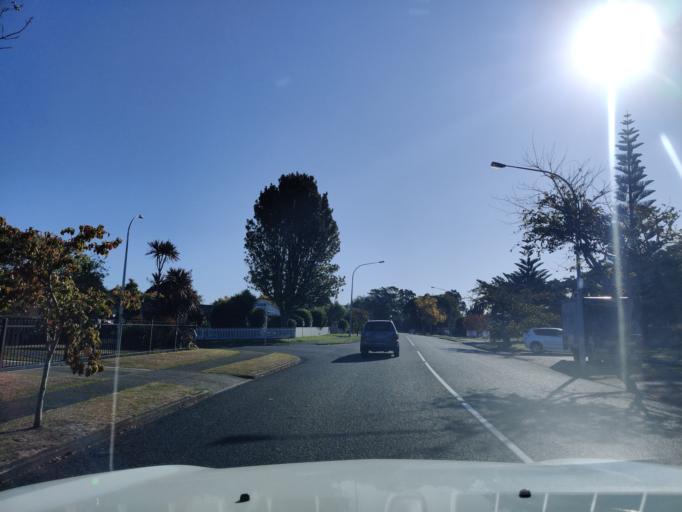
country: NZ
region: Auckland
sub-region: Auckland
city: Takanini
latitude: -37.0437
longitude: 174.9168
